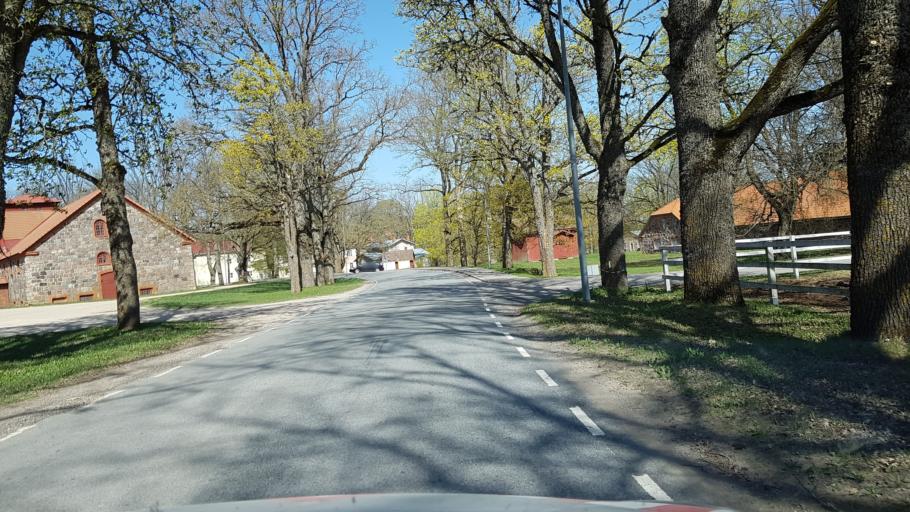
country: EE
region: Viljandimaa
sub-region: Vohma linn
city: Vohma
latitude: 58.5518
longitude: 25.5652
